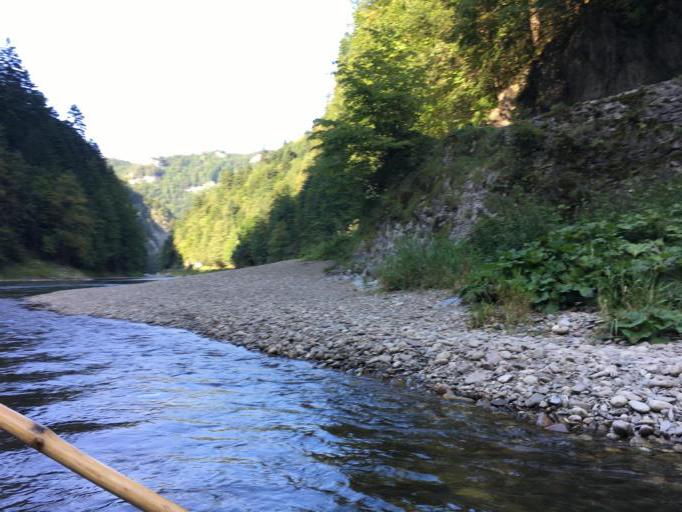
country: PL
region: Lesser Poland Voivodeship
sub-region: Powiat nowotarski
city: Kroscienko nad Dunajcem
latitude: 49.4082
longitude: 20.4290
